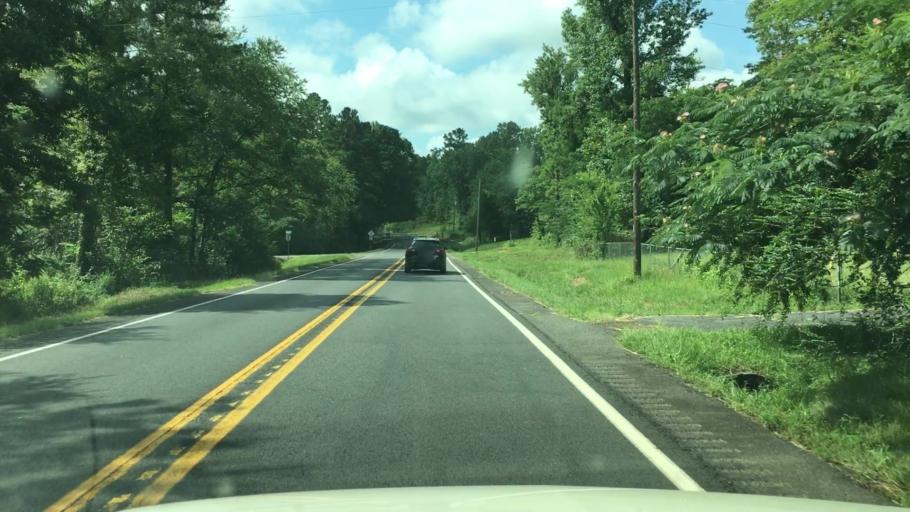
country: US
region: Arkansas
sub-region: Garland County
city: Lake Hamilton
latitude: 34.3494
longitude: -93.1843
